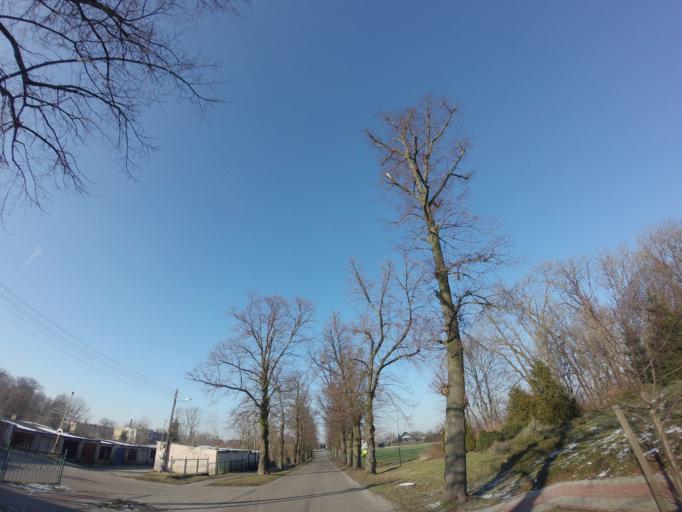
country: PL
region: West Pomeranian Voivodeship
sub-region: Powiat choszczenski
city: Pelczyce
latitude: 53.0973
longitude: 15.3481
